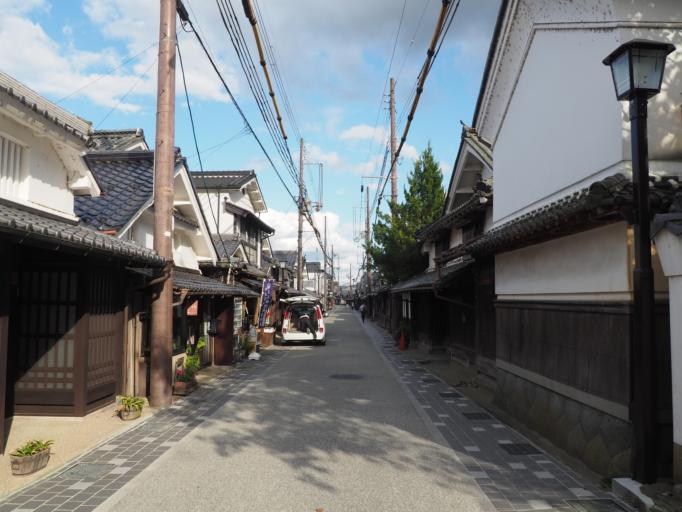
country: JP
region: Hyogo
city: Sasayama
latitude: 35.0716
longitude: 135.2234
